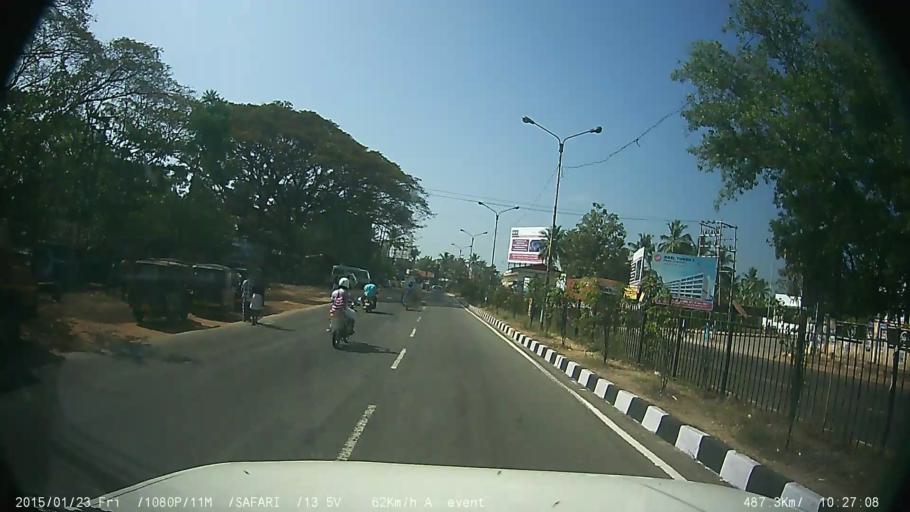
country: IN
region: Kerala
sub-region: Ernakulam
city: Angamali
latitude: 10.1787
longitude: 76.3785
